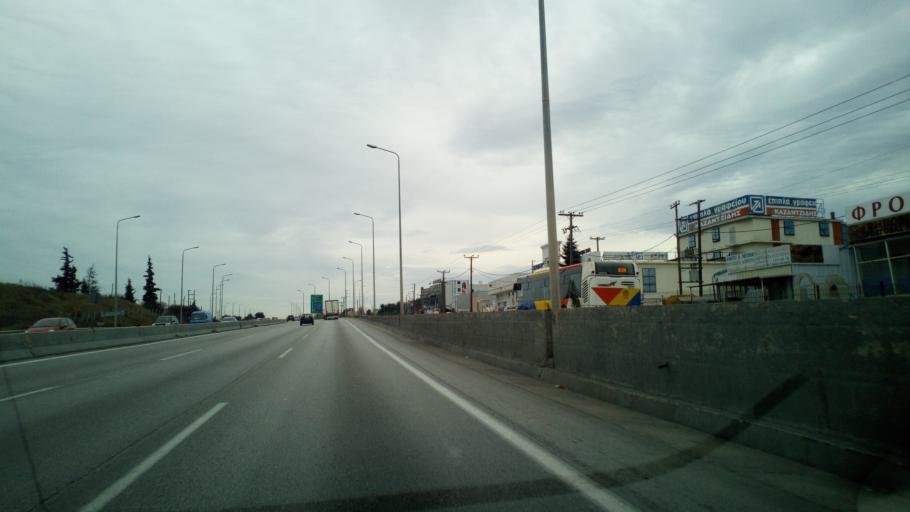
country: GR
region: Central Macedonia
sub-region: Nomos Thessalonikis
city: Liti
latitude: 40.7194
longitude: 22.9708
